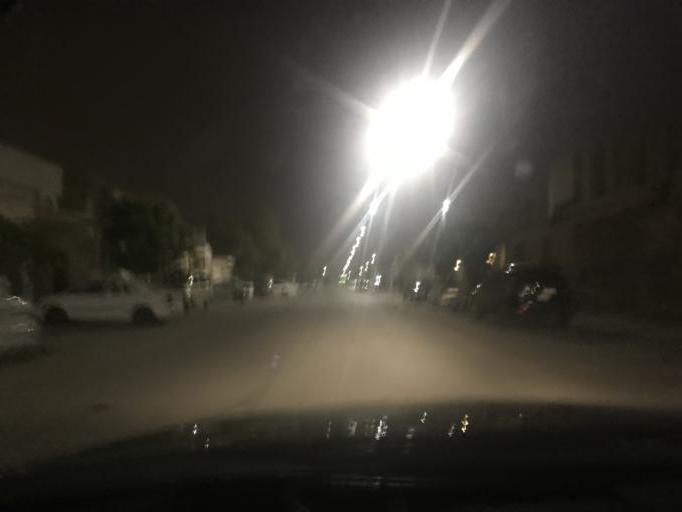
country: SA
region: Ar Riyad
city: Riyadh
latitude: 24.7402
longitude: 46.7715
